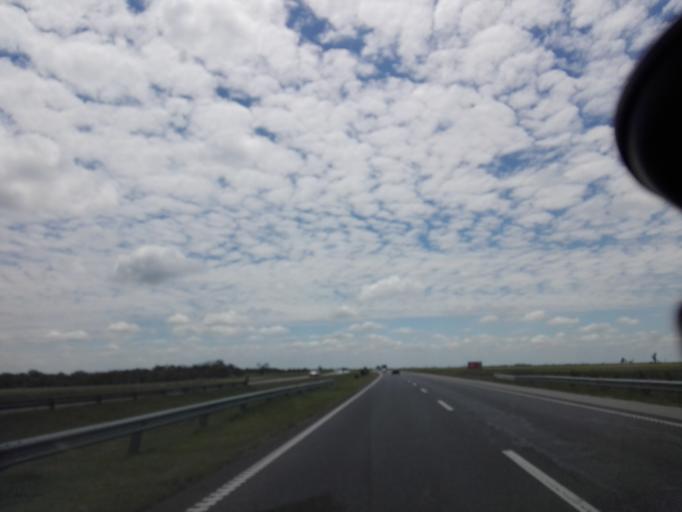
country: AR
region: Cordoba
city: Oliva
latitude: -32.0520
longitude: -63.5079
